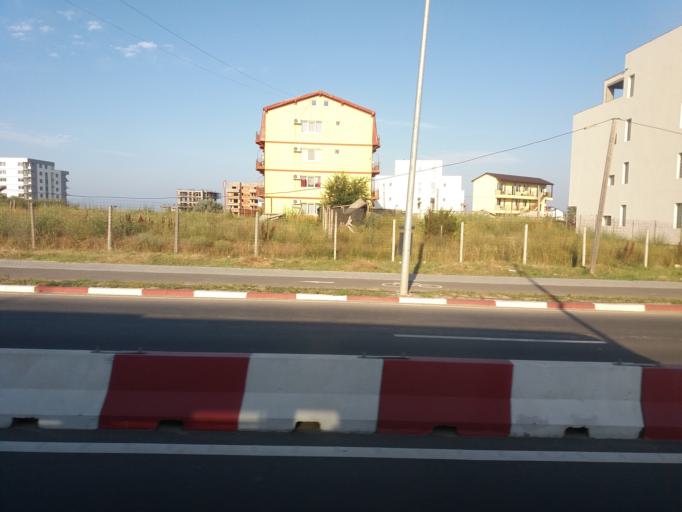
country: RO
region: Constanta
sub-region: Comuna Navodari
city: Navodari
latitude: 44.2928
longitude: 28.6193
